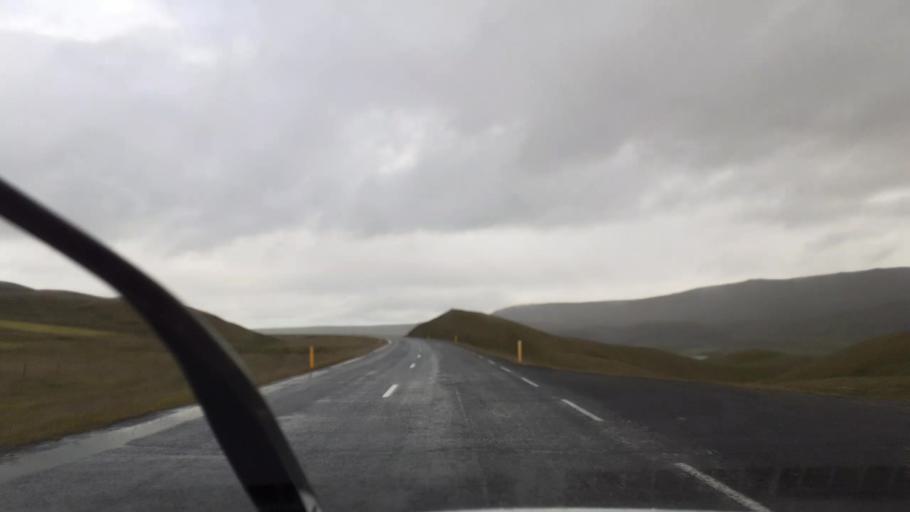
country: IS
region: East
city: Egilsstadir
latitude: 65.3827
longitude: -14.7120
